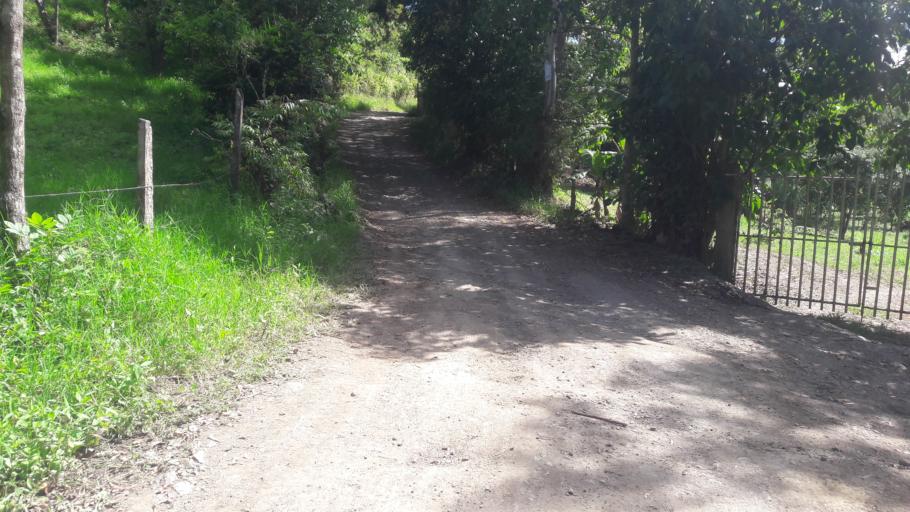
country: CO
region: Cundinamarca
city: Tenza
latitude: 5.0796
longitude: -73.4141
